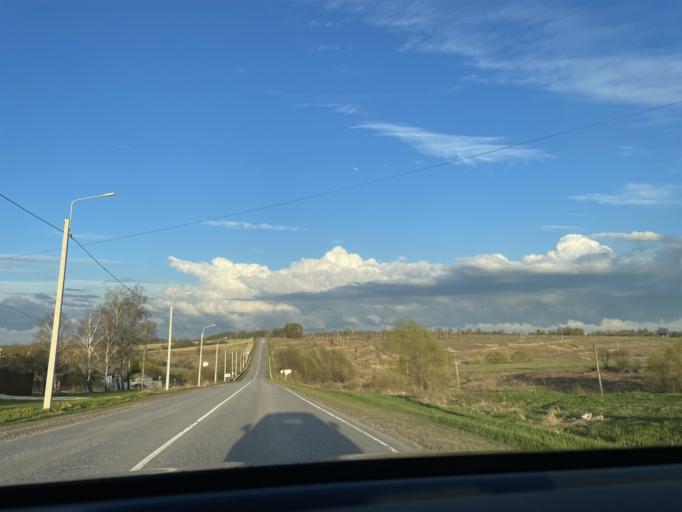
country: RU
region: Tula
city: Novogurovskiy
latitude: 54.5247
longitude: 37.4197
